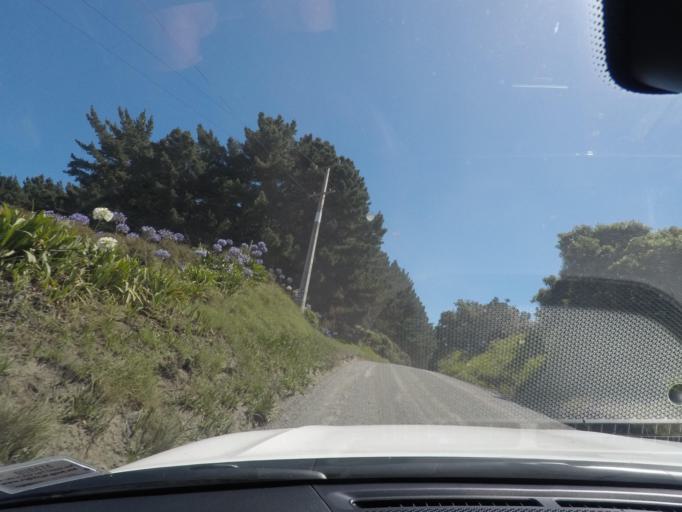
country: NZ
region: Auckland
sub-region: Auckland
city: Parakai
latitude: -36.5832
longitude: 174.2983
